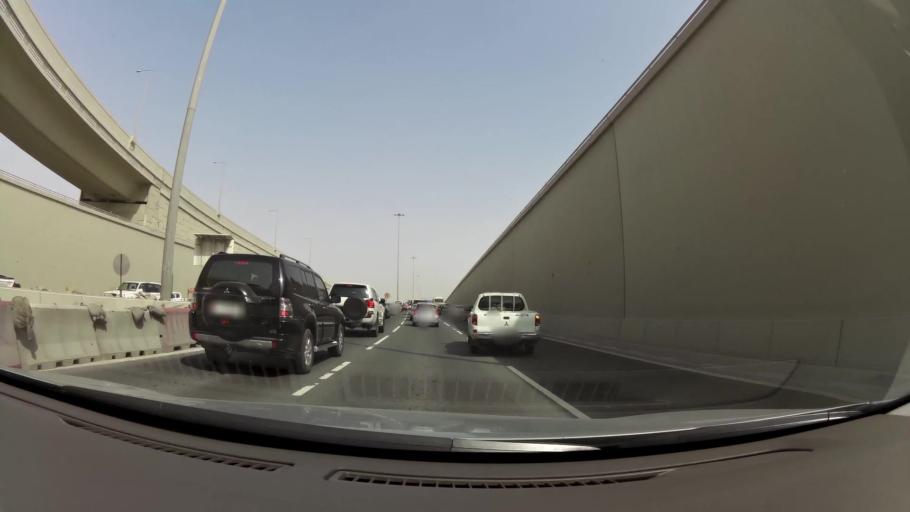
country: QA
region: Baladiyat ad Dawhah
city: Doha
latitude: 25.2964
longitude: 51.4750
